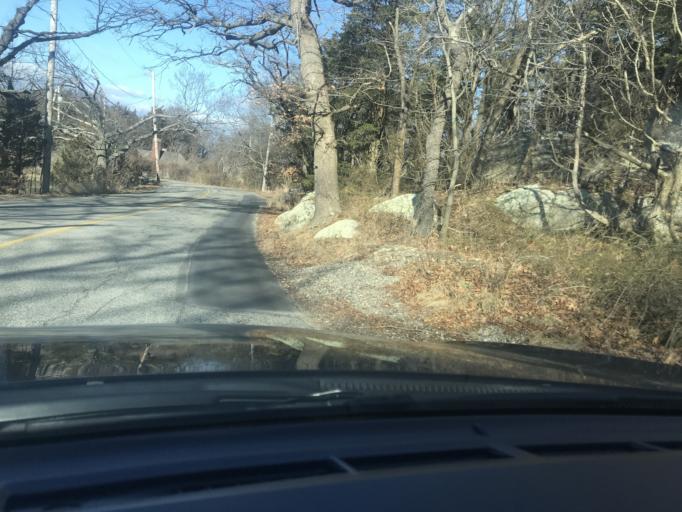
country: US
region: Massachusetts
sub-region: Norfolk County
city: Cohasset
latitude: 42.2536
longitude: -70.7970
